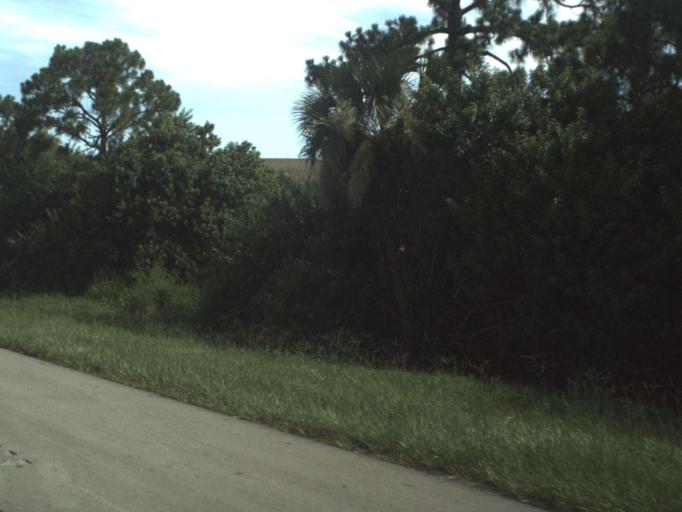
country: US
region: Florida
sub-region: Indian River County
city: West Vero Corridor
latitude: 27.5733
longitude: -80.4923
